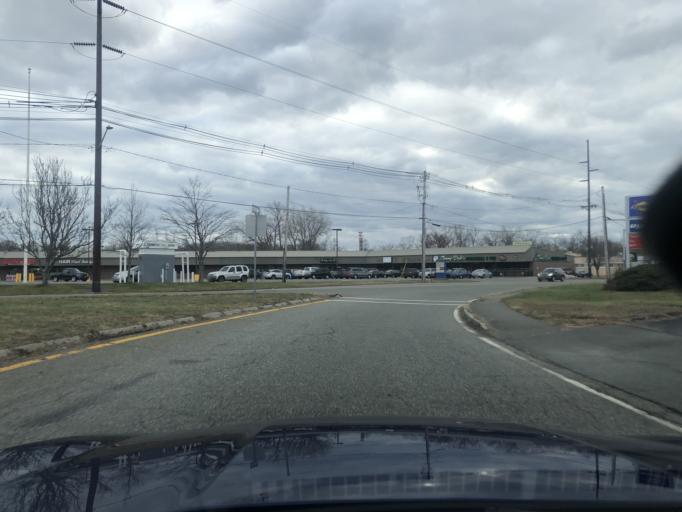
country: US
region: Massachusetts
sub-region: Plymouth County
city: Brockton
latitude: 42.0966
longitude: -71.0090
